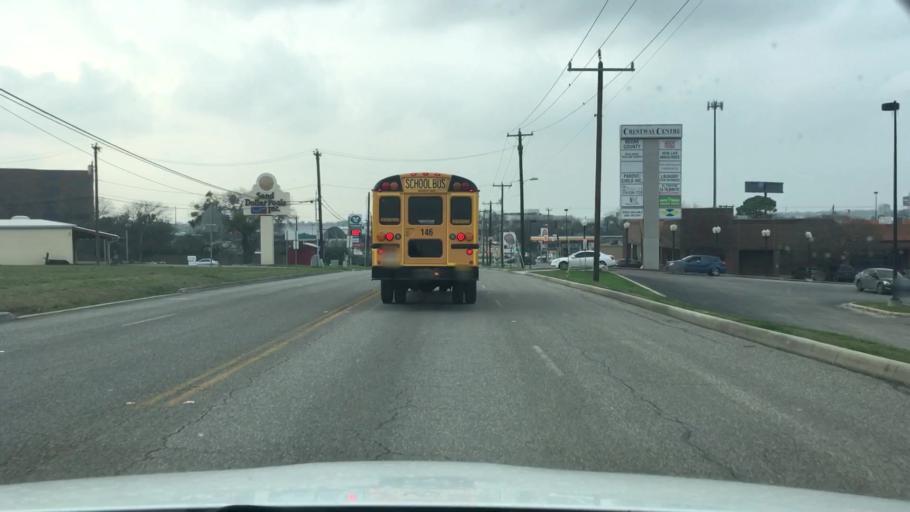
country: US
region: Texas
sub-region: Bexar County
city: Windcrest
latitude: 29.5236
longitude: -98.3880
